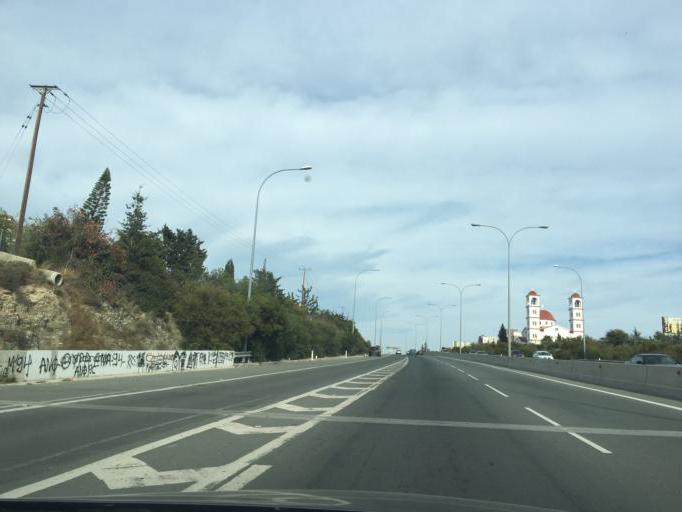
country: CY
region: Limassol
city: Mouttagiaka
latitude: 34.7063
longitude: 33.0948
